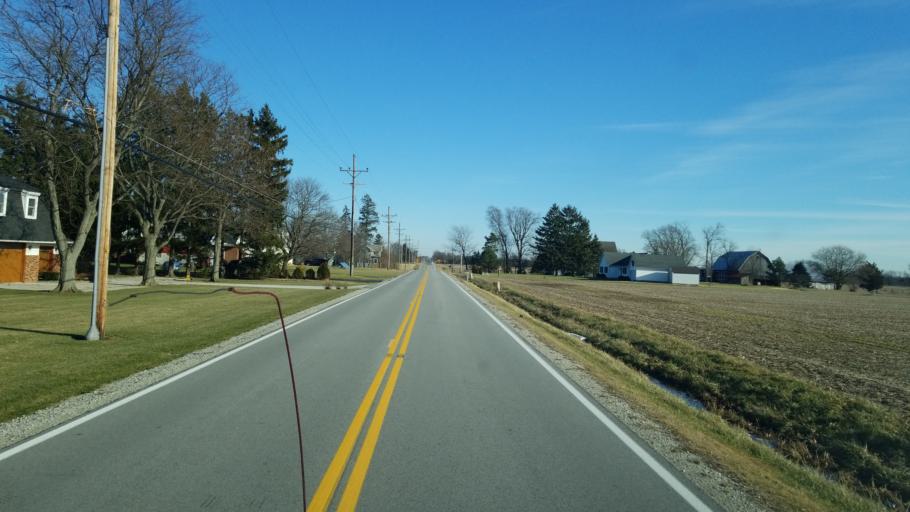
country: US
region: Ohio
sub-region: Sandusky County
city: Stony Prairie
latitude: 41.3493
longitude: -83.1720
